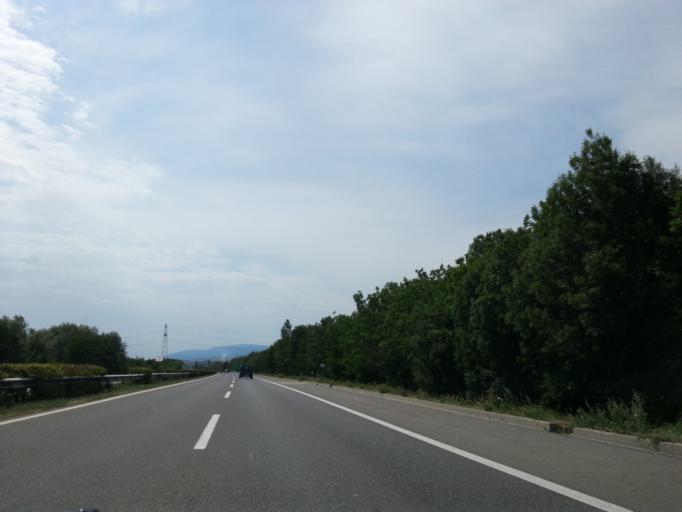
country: CH
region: Vaud
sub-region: Jura-Nord vaudois District
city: Chavornay
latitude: 46.7414
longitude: 6.5875
